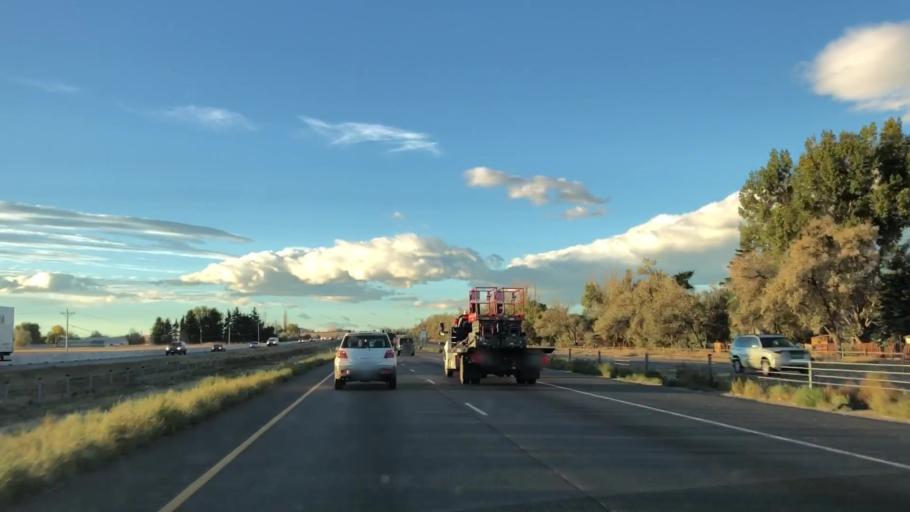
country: US
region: Colorado
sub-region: Weld County
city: Windsor
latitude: 40.4712
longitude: -104.9923
